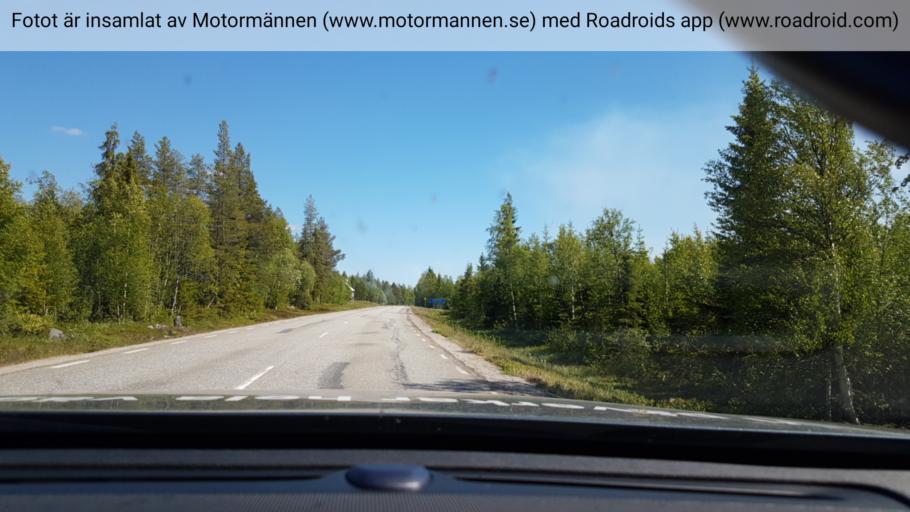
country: SE
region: Vaesterbotten
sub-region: Lycksele Kommun
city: Soderfors
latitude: 64.6827
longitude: 17.8117
